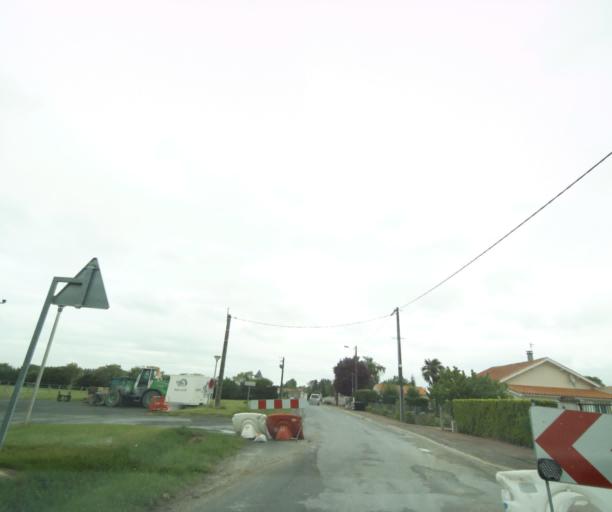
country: FR
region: Poitou-Charentes
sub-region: Departement de la Charente-Maritime
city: Chaniers
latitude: 45.6974
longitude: -0.5283
